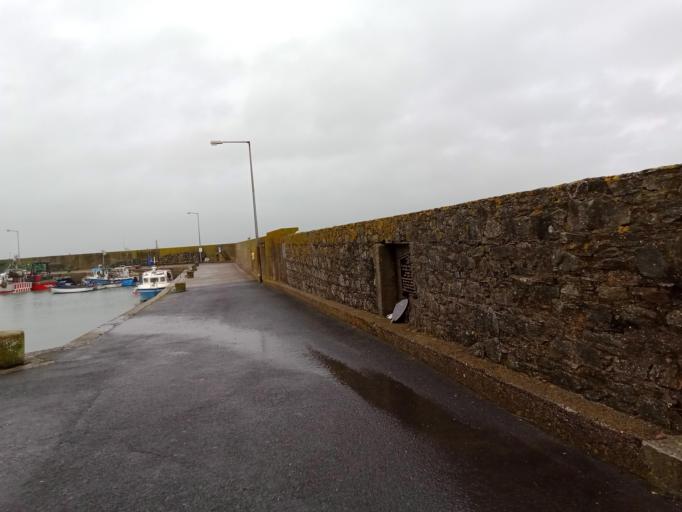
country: IE
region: Munster
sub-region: Waterford
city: Dungarvan
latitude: 52.0547
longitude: -7.5440
